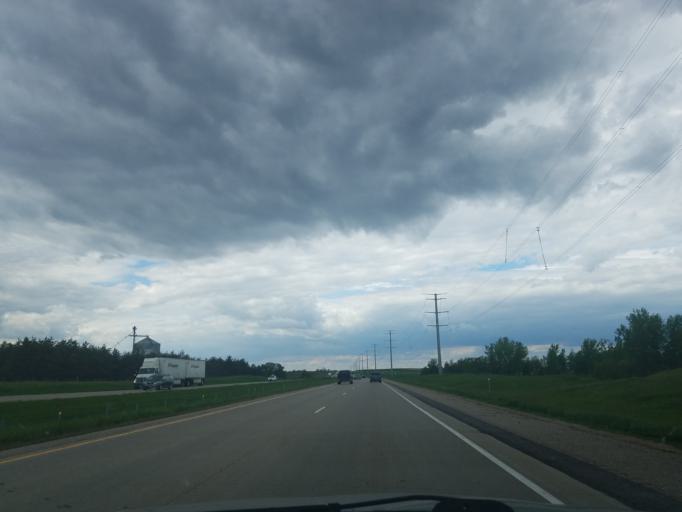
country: US
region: Minnesota
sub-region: Stearns County
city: Sauk Centre
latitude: 45.7741
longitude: -95.0499
